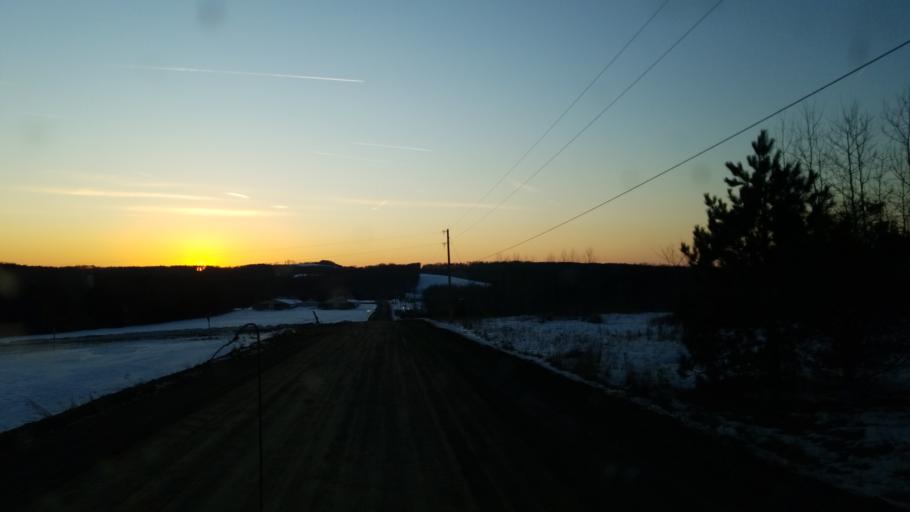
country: US
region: New York
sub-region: Allegany County
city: Andover
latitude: 42.0070
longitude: -77.7122
